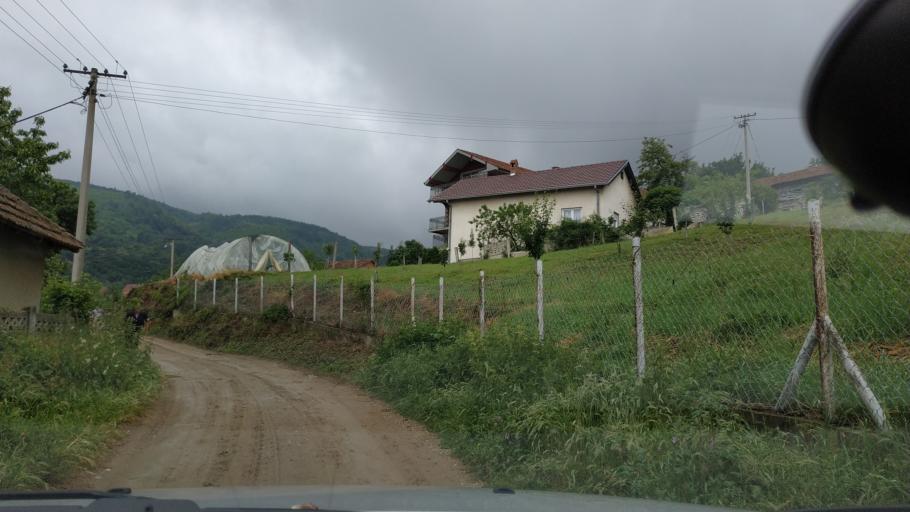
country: RS
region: Central Serbia
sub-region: Toplicki Okrug
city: Prokuplje
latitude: 43.4025
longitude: 21.5542
